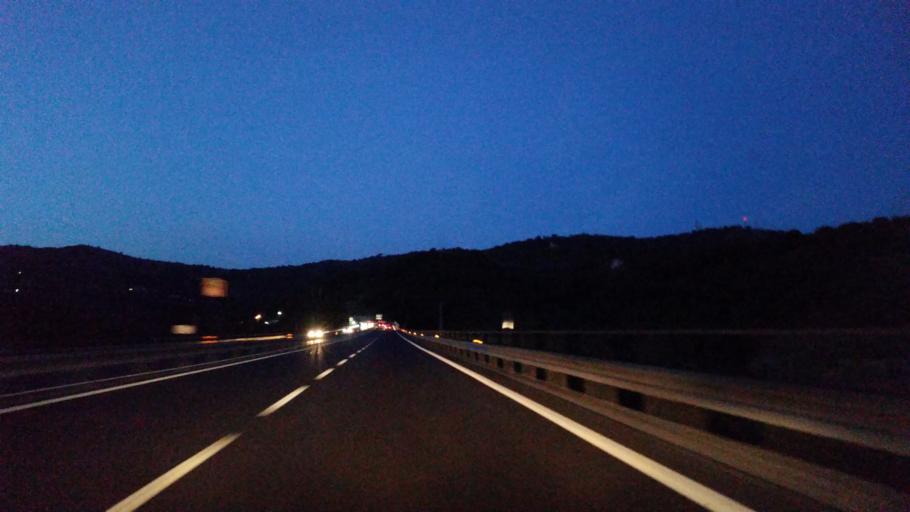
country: IT
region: Liguria
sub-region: Provincia di Imperia
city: San Bartolomeo al Mare
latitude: 43.9326
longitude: 8.1024
